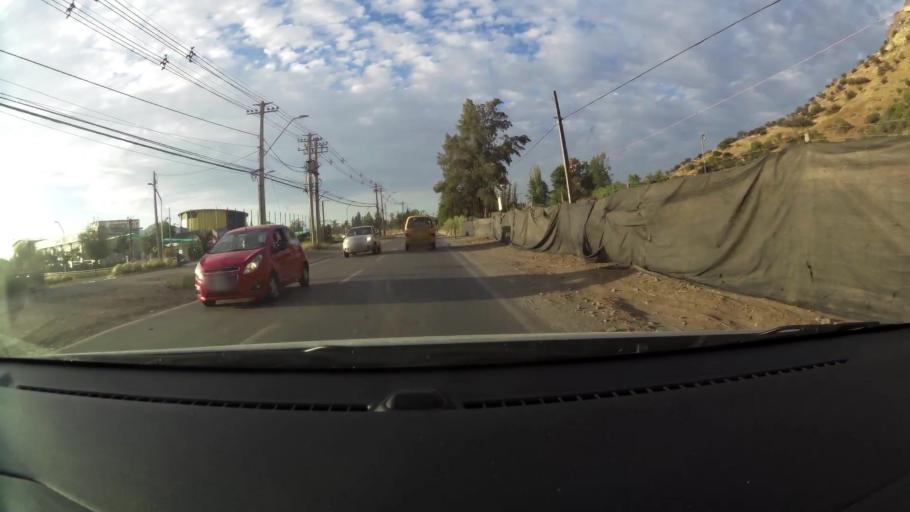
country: CL
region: Santiago Metropolitan
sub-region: Provincia de Maipo
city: San Bernardo
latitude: -33.6259
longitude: -70.6799
